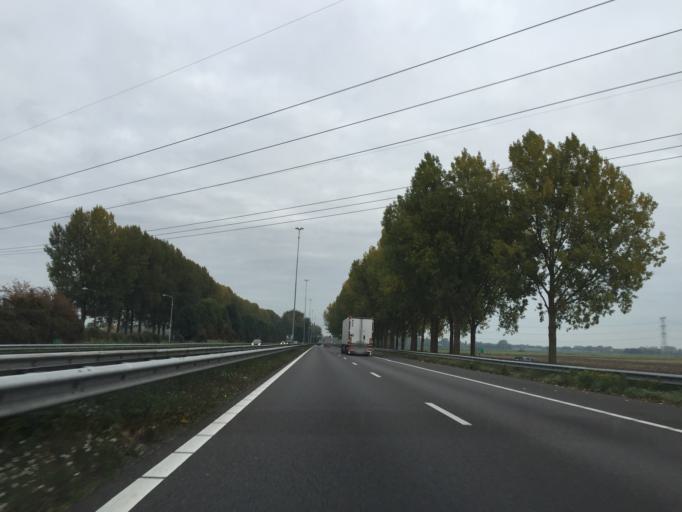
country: NL
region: North Brabant
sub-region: Gemeente Oosterhout
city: Oosterhout
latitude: 51.6659
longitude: 4.8804
